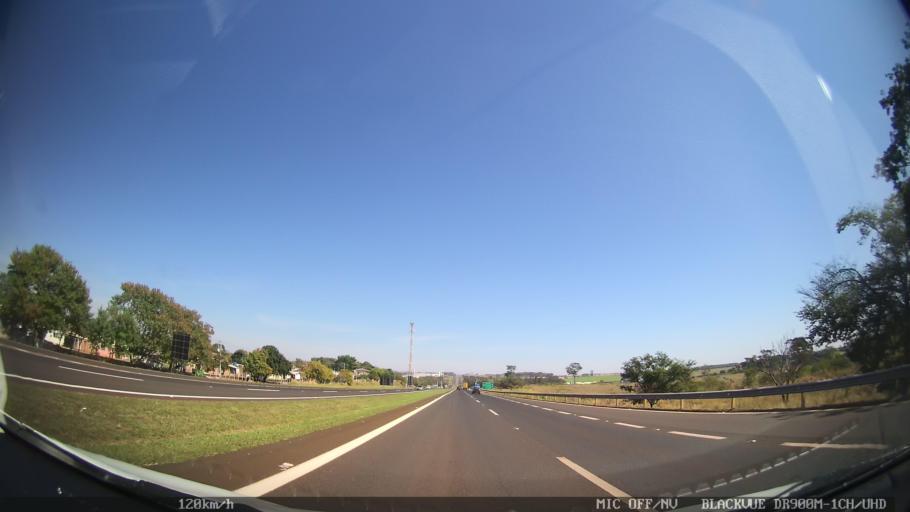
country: BR
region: Sao Paulo
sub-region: Ribeirao Preto
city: Ribeirao Preto
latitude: -21.1026
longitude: -47.8032
